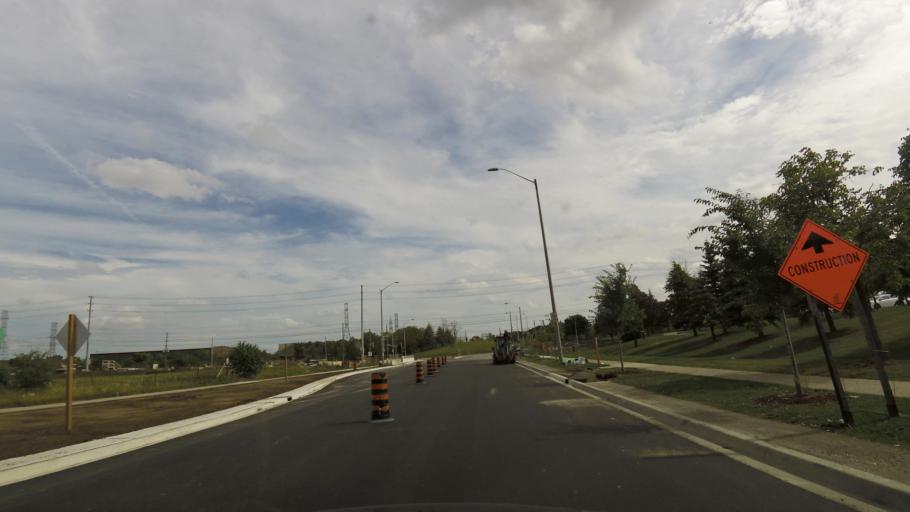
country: CA
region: Ontario
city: Etobicoke
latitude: 43.6607
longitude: -79.5956
